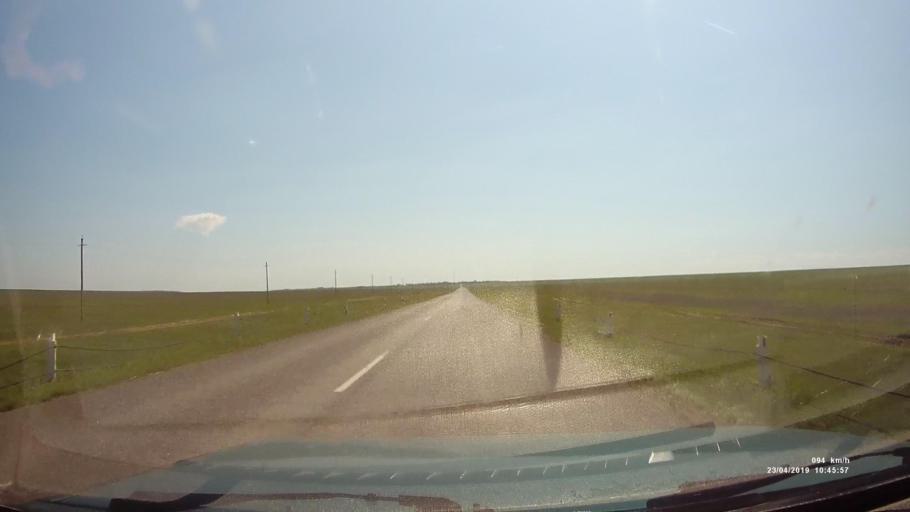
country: RU
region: Kalmykiya
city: Yashalta
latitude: 46.4470
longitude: 42.6831
